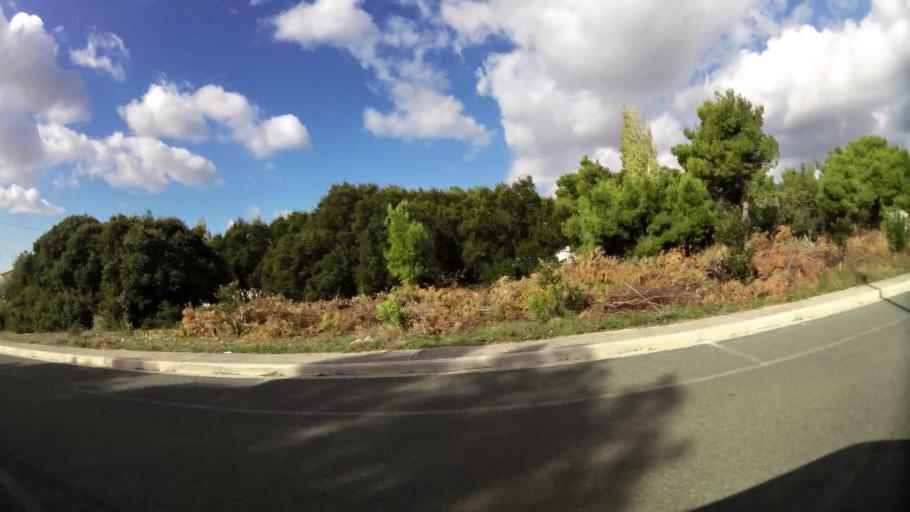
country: GR
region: Attica
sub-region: Nomarchia Anatolikis Attikis
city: Thrakomakedones
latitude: 38.1254
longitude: 23.7671
